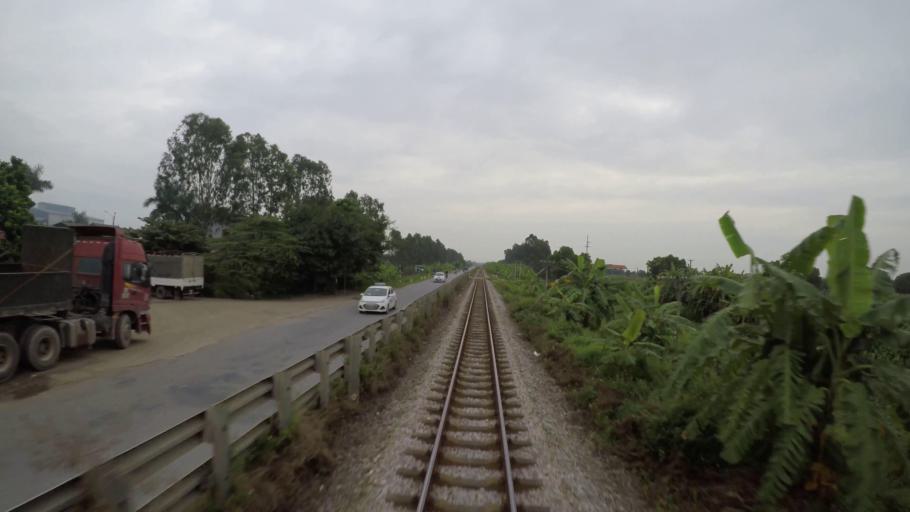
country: VN
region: Hung Yen
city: Ban Yen Nhan
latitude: 20.9853
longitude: 106.0657
